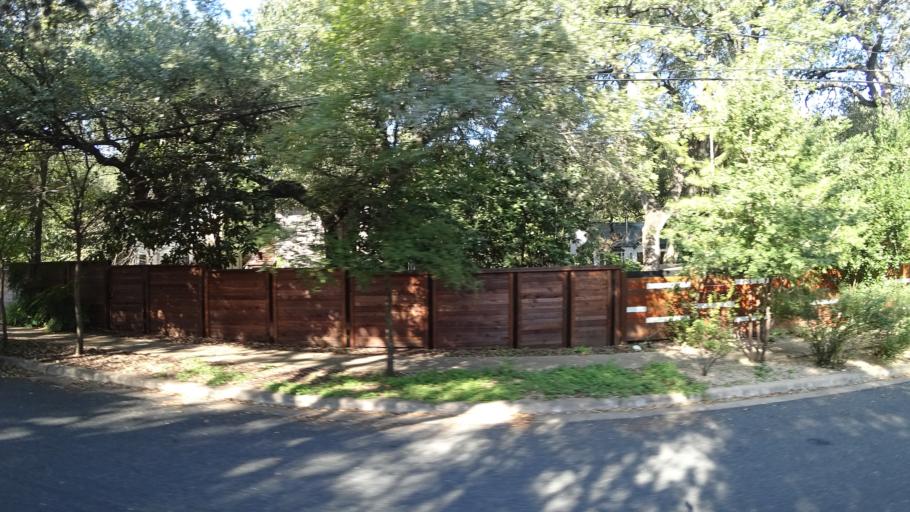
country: US
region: Texas
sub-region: Travis County
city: Austin
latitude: 30.2499
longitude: -97.7463
